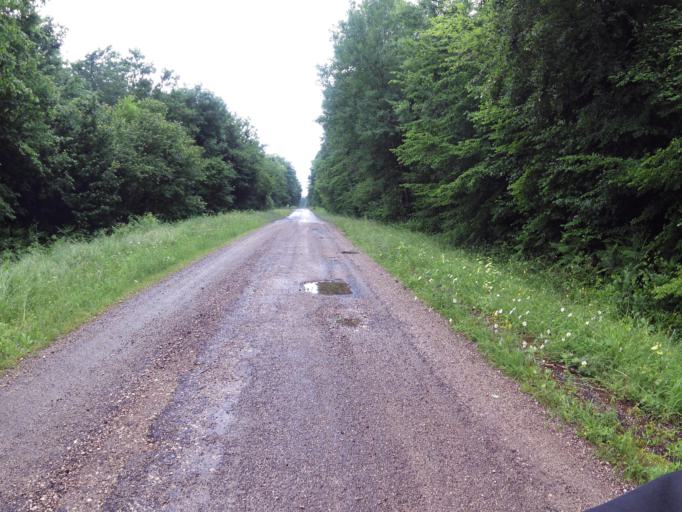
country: FR
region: Champagne-Ardenne
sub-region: Departement de la Marne
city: Sermaize-les-Bains
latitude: 48.7621
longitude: 4.9475
